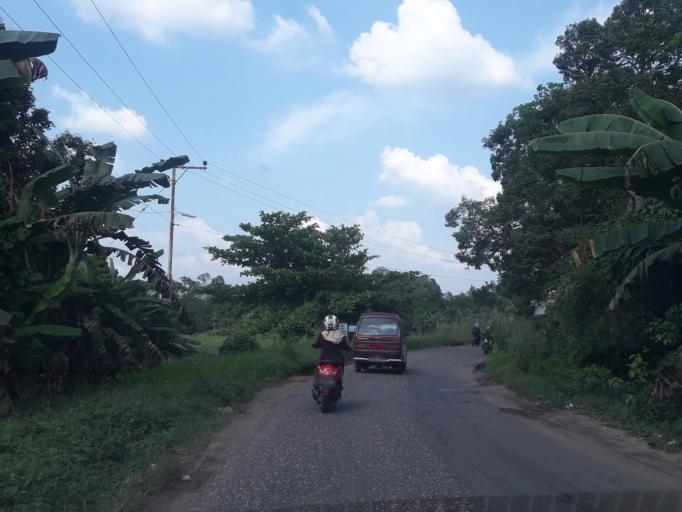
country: ID
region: South Kalimantan
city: Pasararba
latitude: -2.2048
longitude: 115.3313
